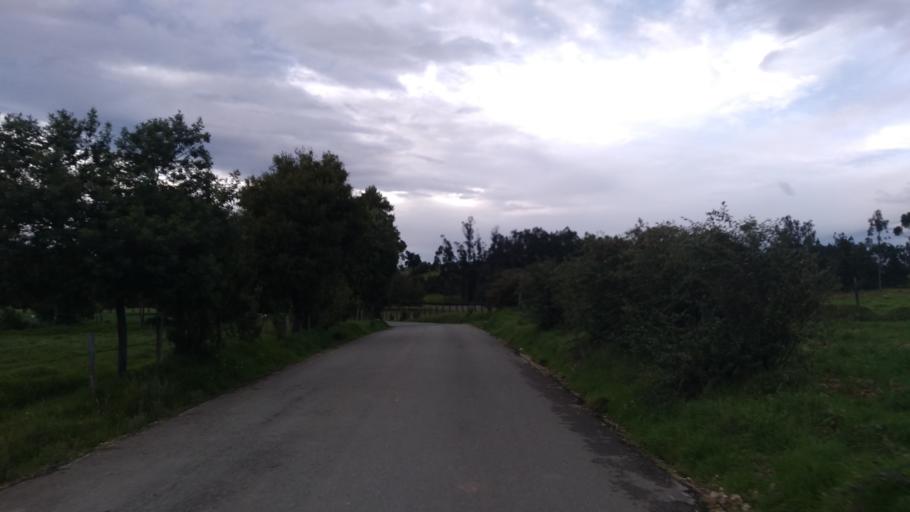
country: CO
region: Boyaca
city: Toca
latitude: 5.5933
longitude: -73.1802
